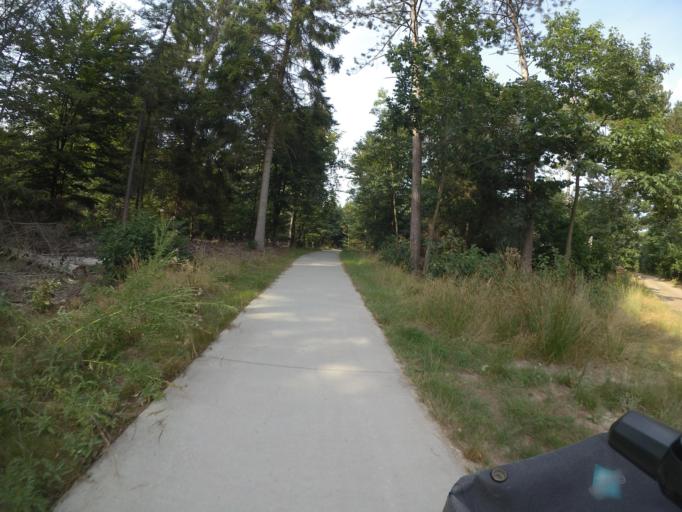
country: NL
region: Drenthe
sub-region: Gemeente Westerveld
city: Dwingeloo
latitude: 52.9032
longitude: 6.3638
